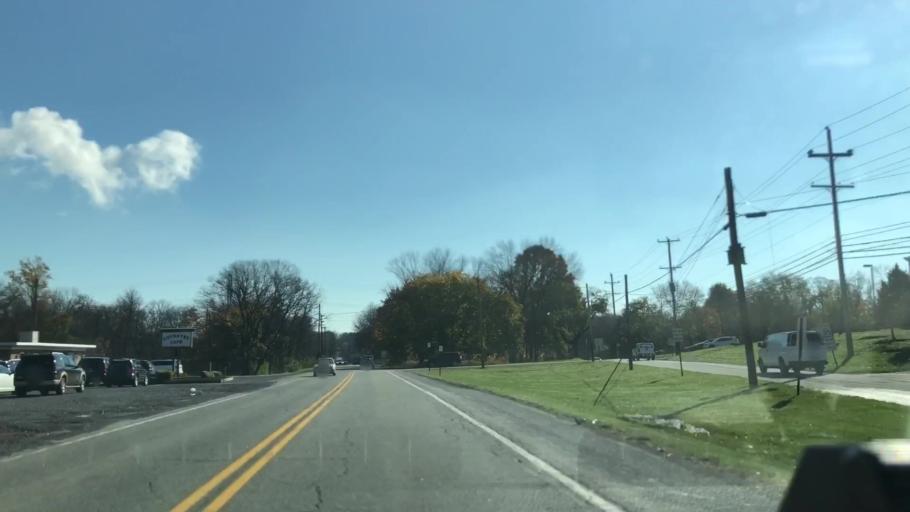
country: US
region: Pennsylvania
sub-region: Chester County
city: Kenilworth
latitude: 40.2269
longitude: -75.6227
